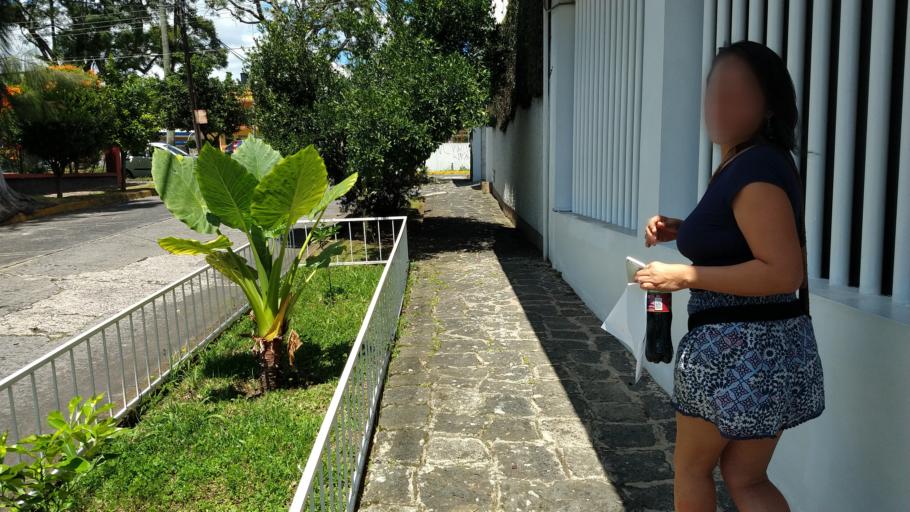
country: MX
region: Veracruz
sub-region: Xalapa
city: Xalapa de Enriquez
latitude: 19.5390
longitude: -96.9289
